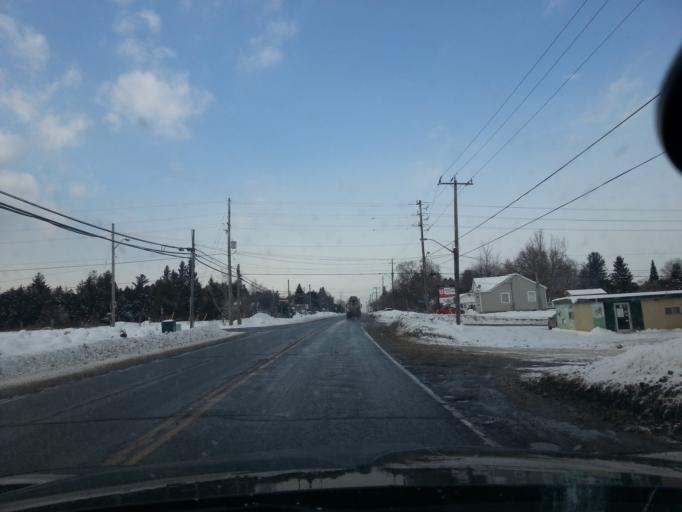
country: CA
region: Ontario
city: Bells Corners
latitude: 45.2721
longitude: -75.9456
